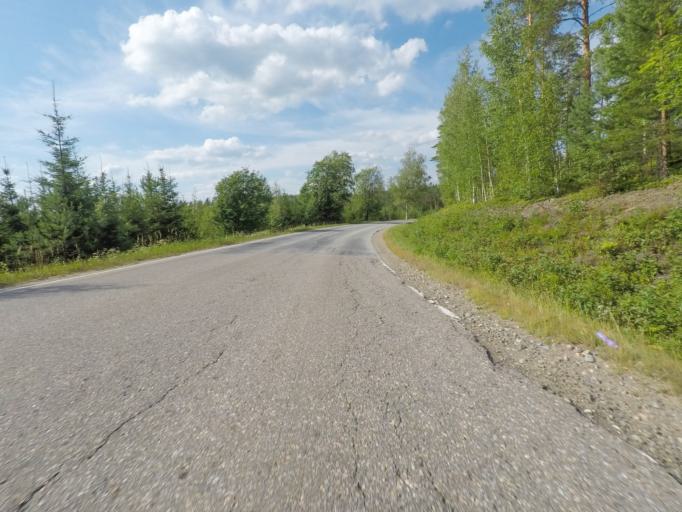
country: FI
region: Southern Savonia
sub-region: Mikkeli
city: Puumala
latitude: 61.6919
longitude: 28.2160
